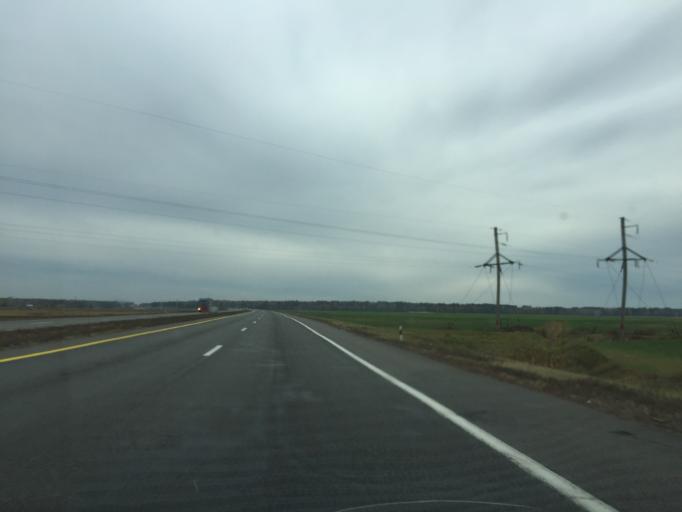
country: BY
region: Gomel
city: Horad Rechytsa
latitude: 52.3450
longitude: 30.5675
